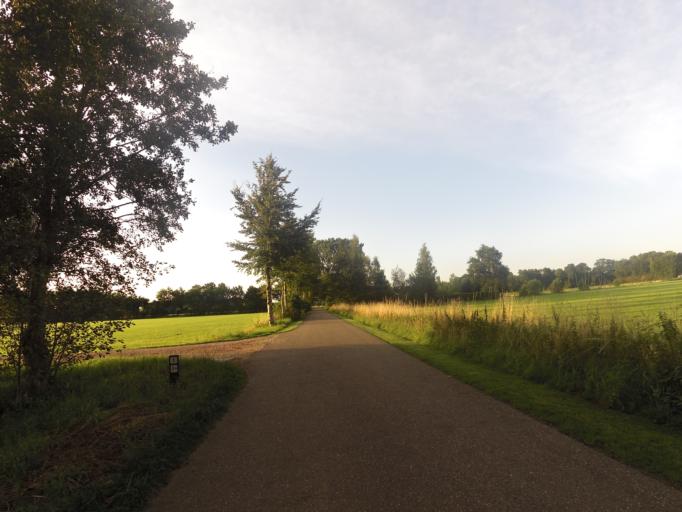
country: NL
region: Gelderland
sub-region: Oude IJsselstreek
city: Varsseveld
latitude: 51.8914
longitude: 6.4820
